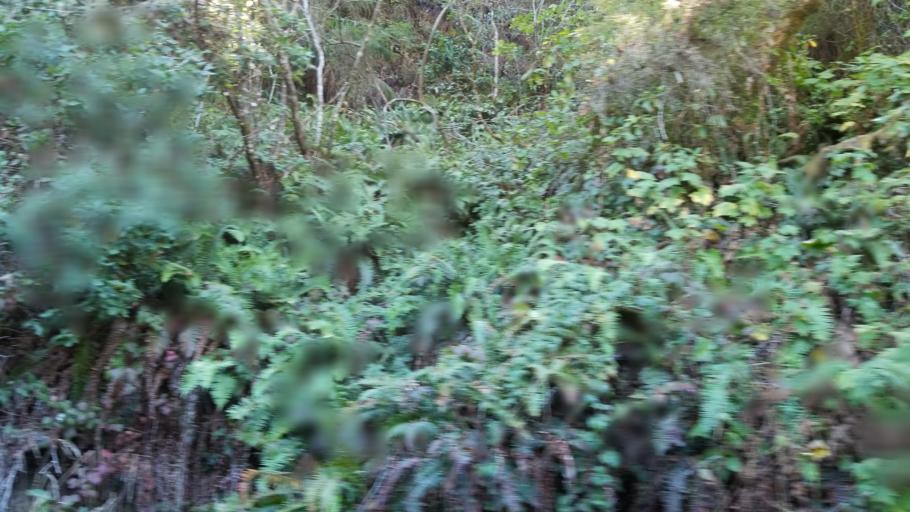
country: US
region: California
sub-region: Mendocino County
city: Fort Bragg
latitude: 39.4464
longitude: -123.7910
